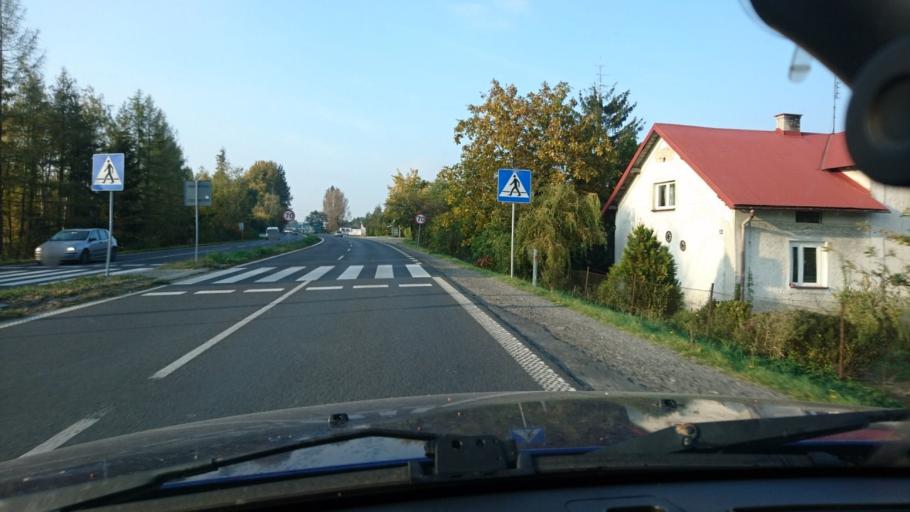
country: PL
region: Silesian Voivodeship
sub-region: Powiat cieszynski
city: Gorki Wielkie
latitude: 49.7781
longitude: 18.8088
